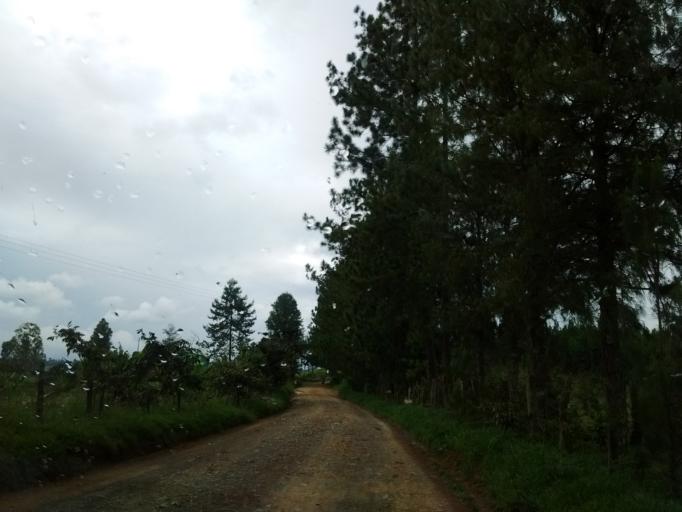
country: CO
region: Cauca
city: Cajibio
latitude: 2.5836
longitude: -76.6780
